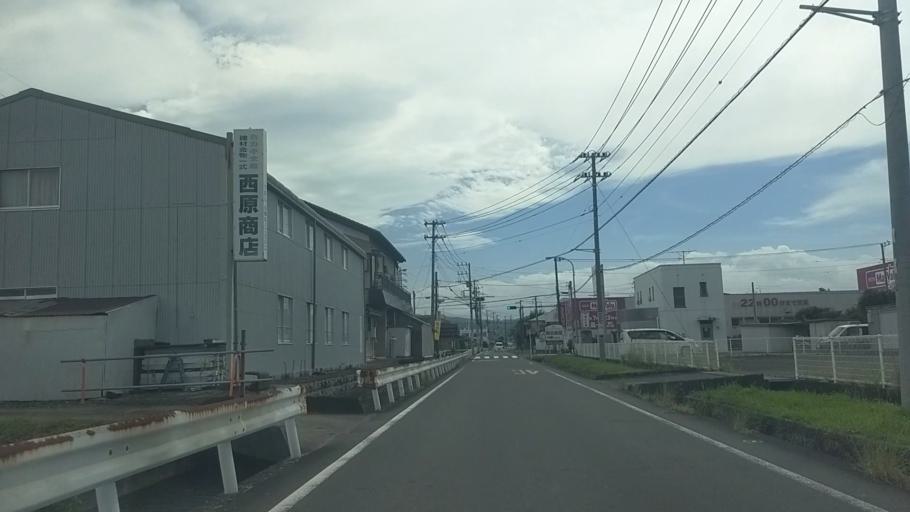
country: JP
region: Shizuoka
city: Mishima
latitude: 35.0587
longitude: 138.9485
